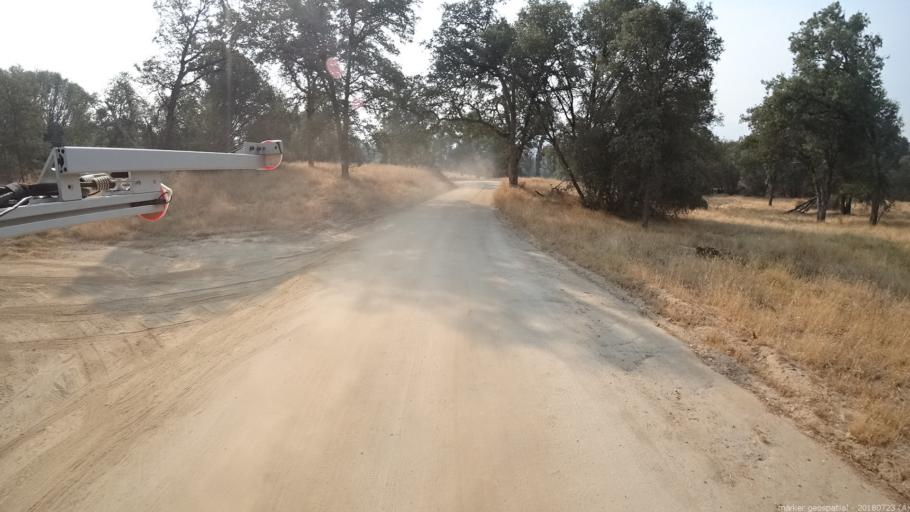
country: US
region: California
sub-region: Madera County
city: Ahwahnee
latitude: 37.3650
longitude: -119.7121
